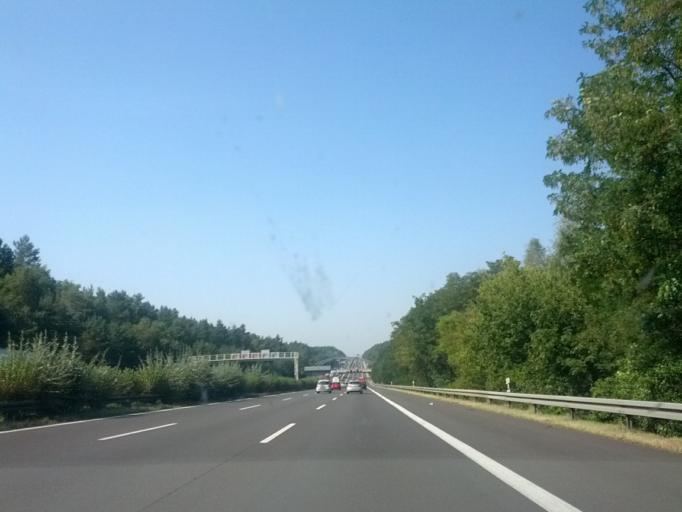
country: DE
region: Brandenburg
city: Michendorf
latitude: 52.3025
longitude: 12.9701
